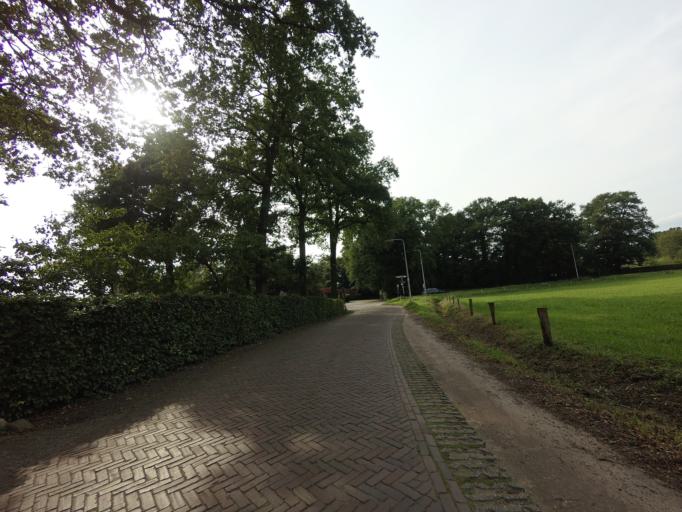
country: DE
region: Lower Saxony
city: Getelo
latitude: 52.4428
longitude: 6.8251
